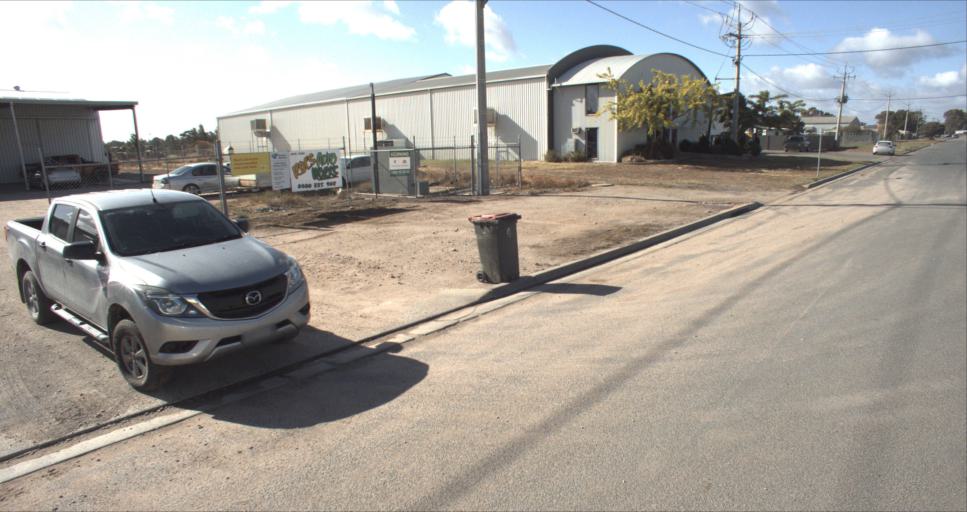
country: AU
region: New South Wales
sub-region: Leeton
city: Leeton
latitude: -34.5459
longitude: 146.3911
